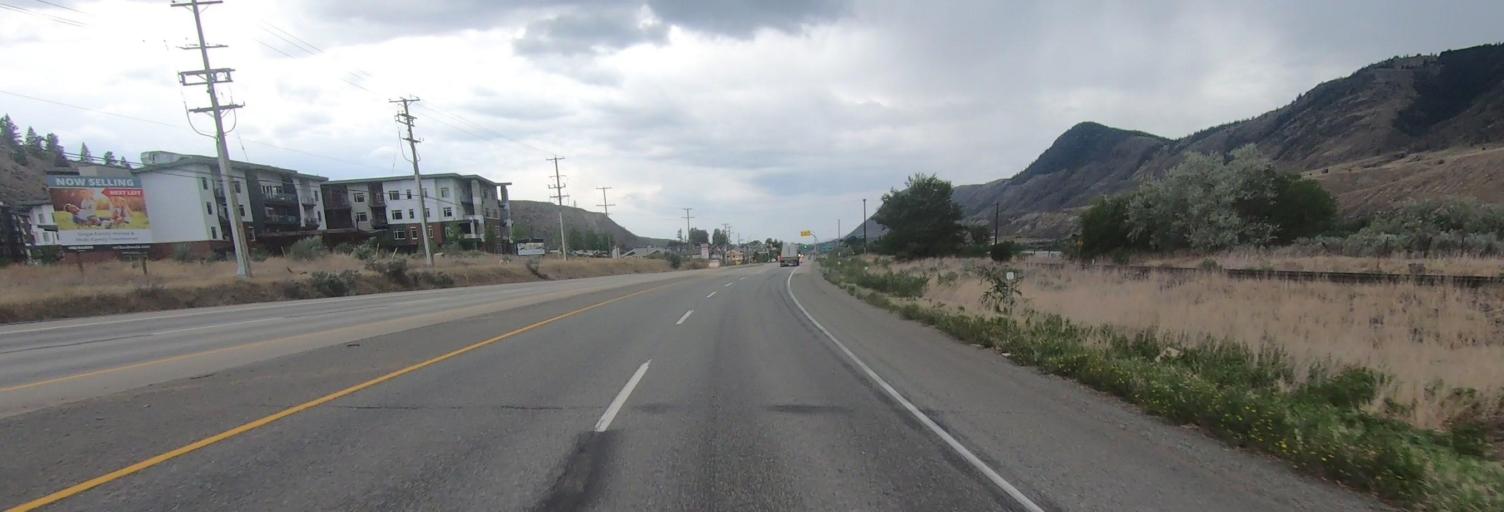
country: CA
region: British Columbia
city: Kamloops
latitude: 50.6711
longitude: -120.2218
